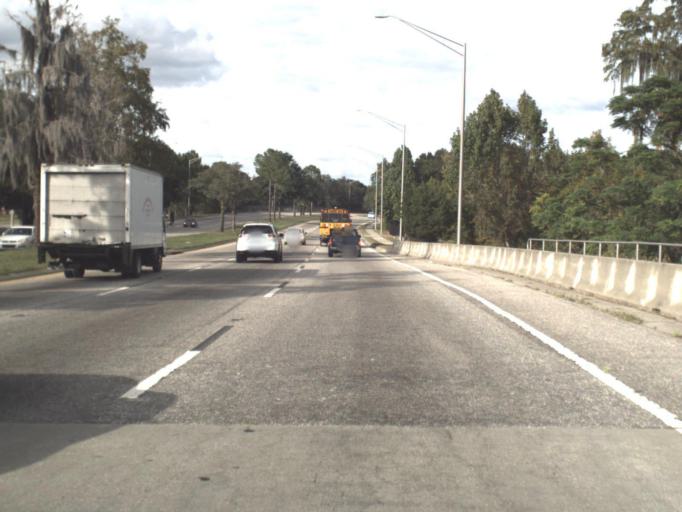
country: US
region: Florida
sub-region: Orange County
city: Holden Heights
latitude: 28.5215
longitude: -81.4174
